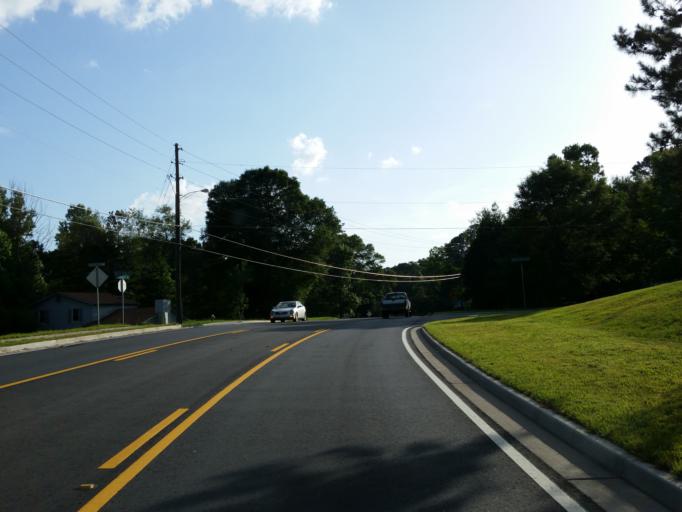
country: US
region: Georgia
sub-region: Cherokee County
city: Woodstock
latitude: 34.0650
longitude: -84.5540
